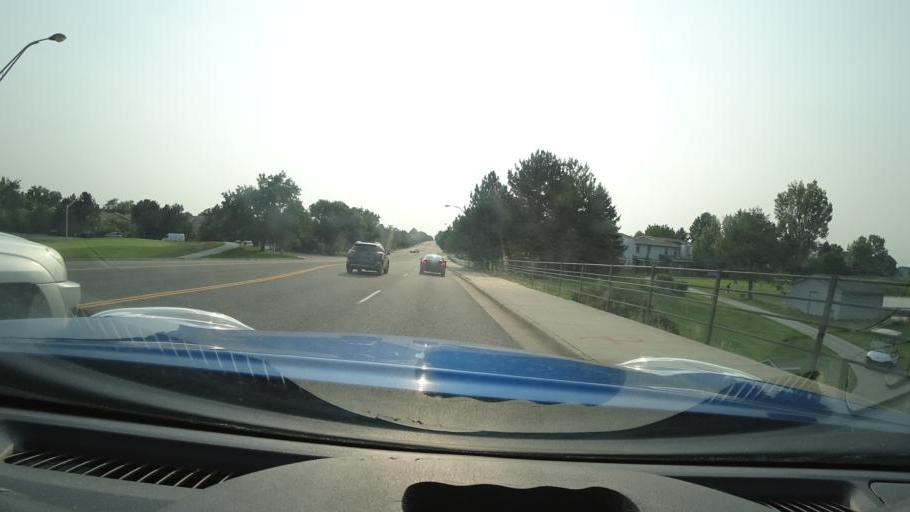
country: US
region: Colorado
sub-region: Adams County
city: Aurora
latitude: 39.6677
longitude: -104.8347
